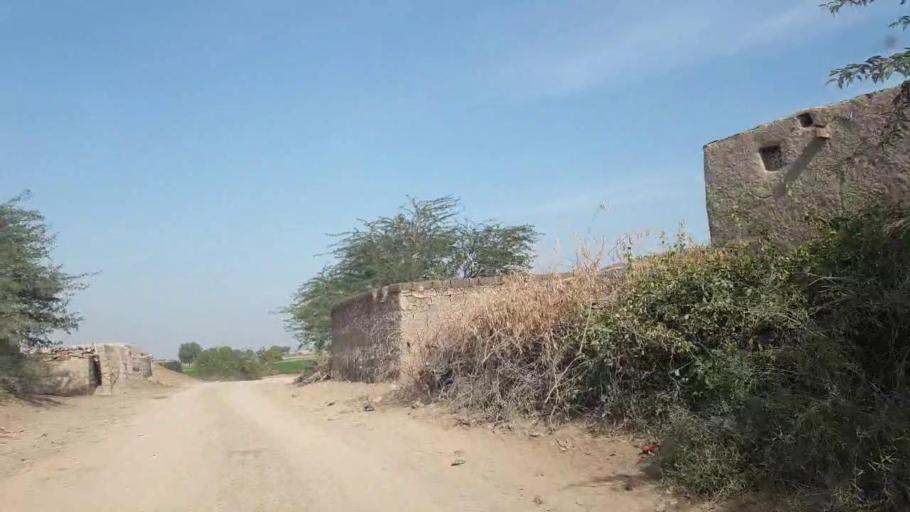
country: PK
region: Sindh
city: Hala
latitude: 25.7585
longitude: 68.2953
